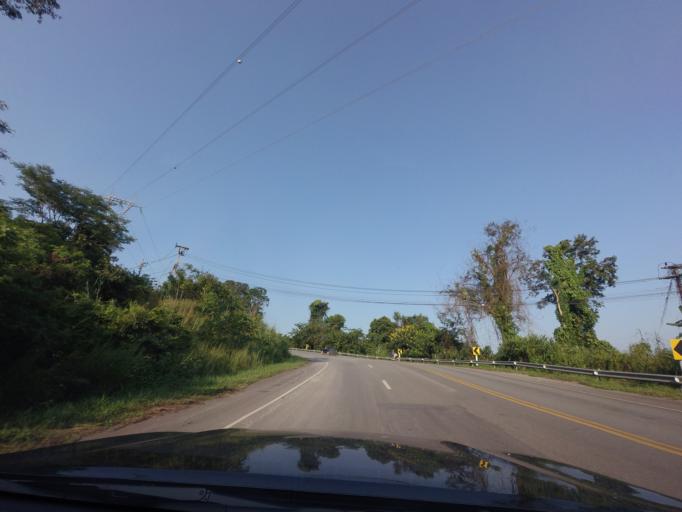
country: TH
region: Loei
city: Dan Sai
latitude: 17.2229
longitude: 101.1478
